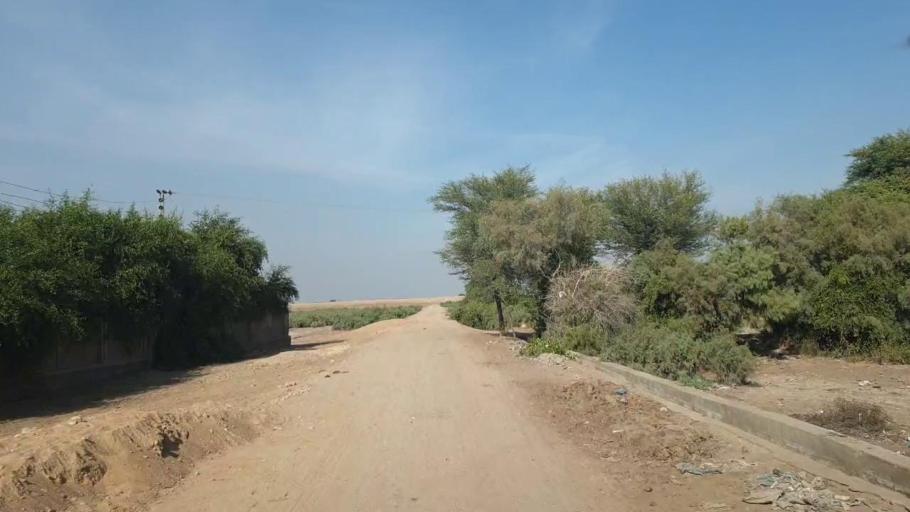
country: PK
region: Sindh
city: Sann
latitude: 25.9104
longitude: 68.2350
